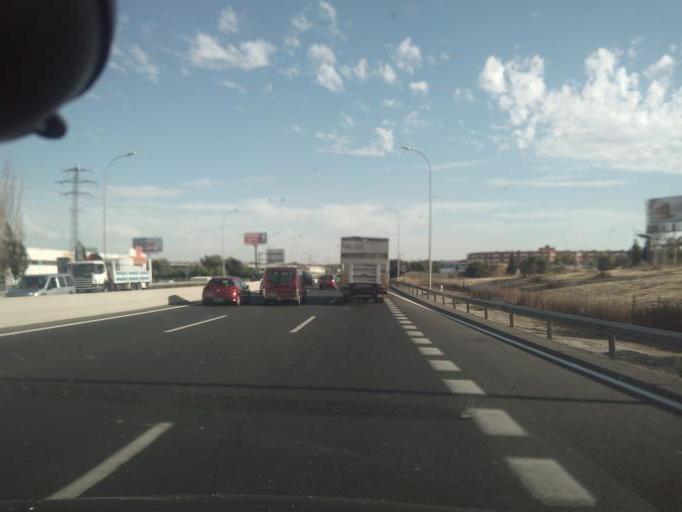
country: ES
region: Madrid
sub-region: Provincia de Madrid
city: Pinto
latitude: 40.2633
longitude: -3.6905
